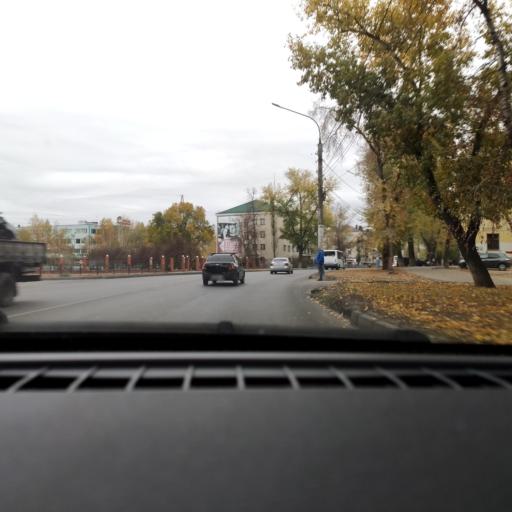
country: RU
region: Voronezj
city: Somovo
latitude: 51.7193
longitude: 39.2733
